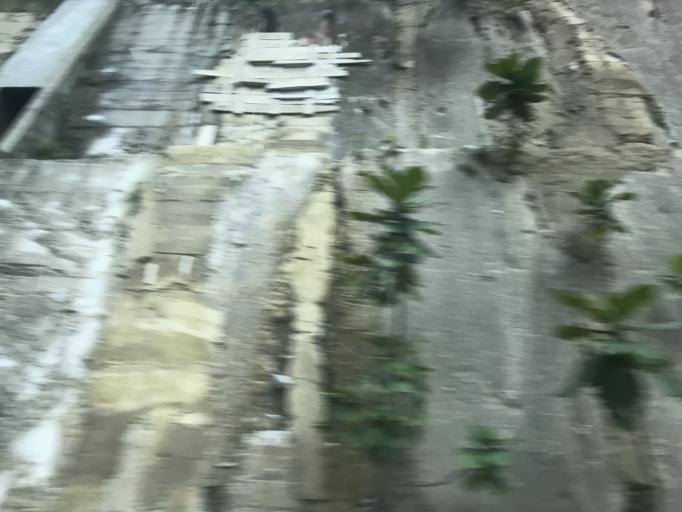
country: GT
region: Chimaltenango
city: El Tejar
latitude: 14.6383
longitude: -90.7899
